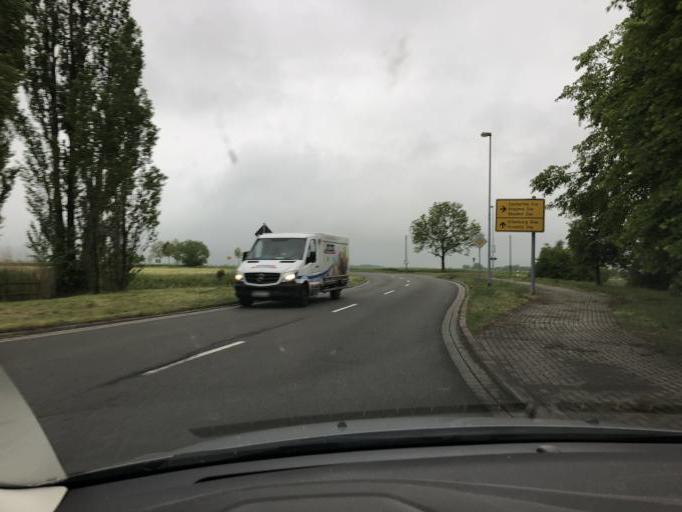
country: DE
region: Saxony
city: Krostitz
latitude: 51.4837
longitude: 12.4158
